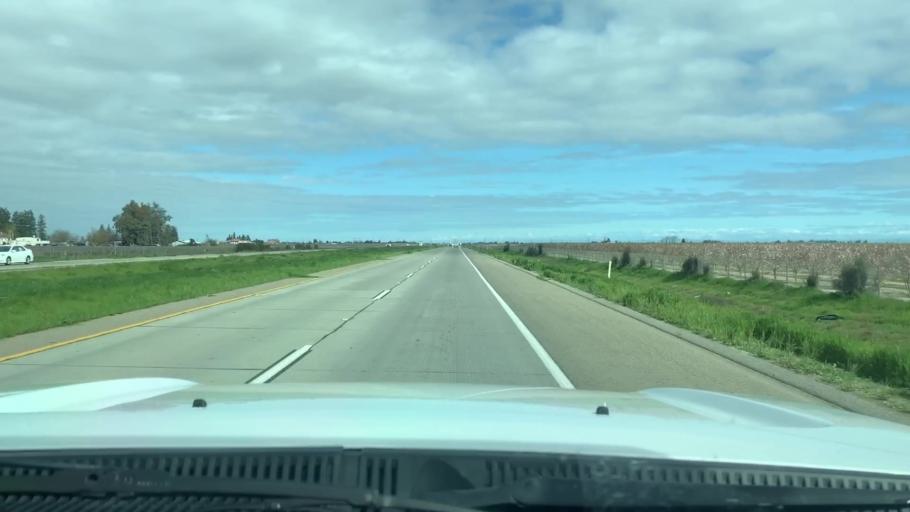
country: US
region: California
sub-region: Fresno County
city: Caruthers
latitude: 36.5513
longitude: -119.7860
